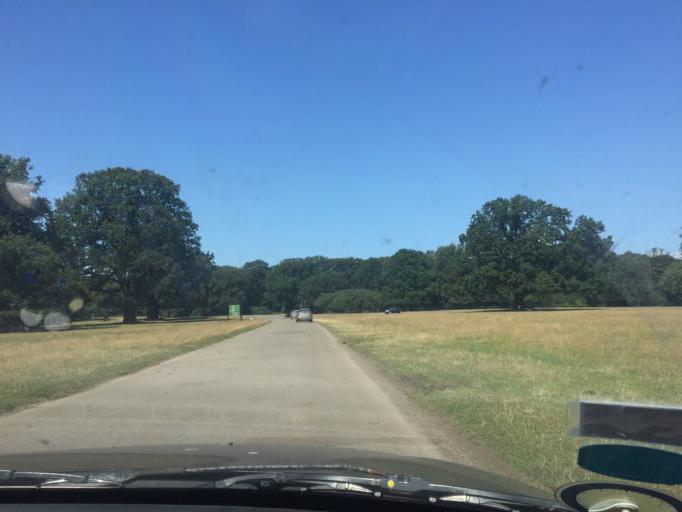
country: DK
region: Zealand
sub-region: Lolland Kommune
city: Maribo
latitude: 54.8251
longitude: 11.5020
